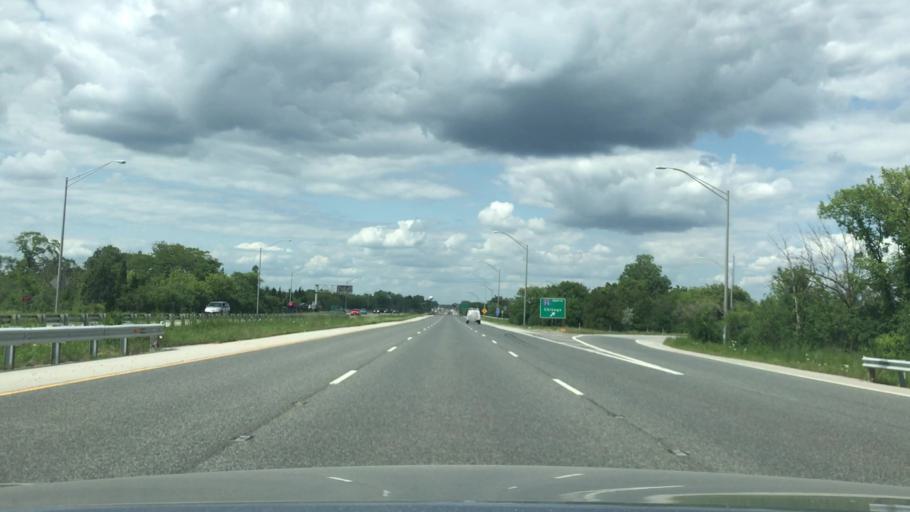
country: US
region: Illinois
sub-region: DuPage County
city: Burr Ridge
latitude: 41.7383
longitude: -87.9442
